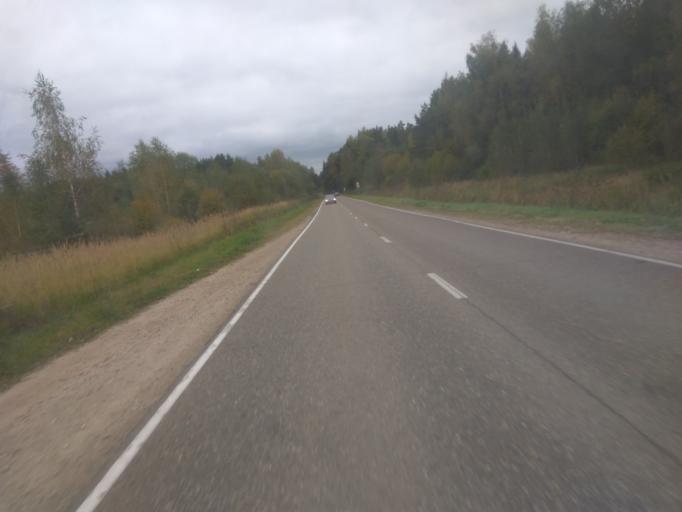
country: RU
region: Moskovskaya
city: Chupryakovo
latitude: 55.5990
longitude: 36.6200
